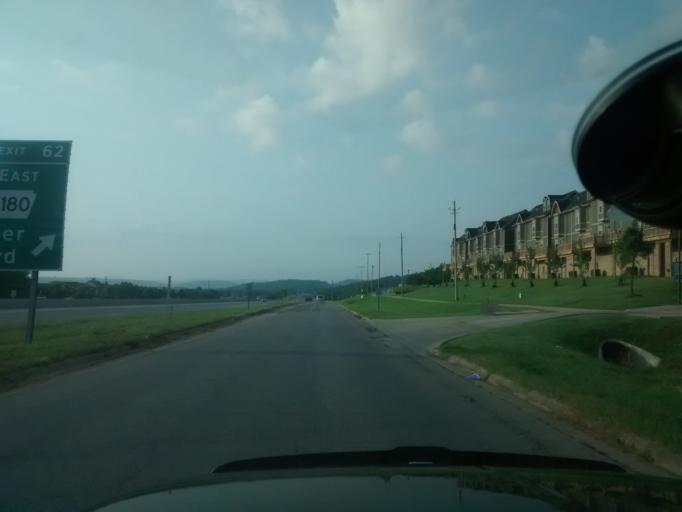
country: US
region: Arkansas
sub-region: Washington County
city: Fayetteville
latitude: 36.0624
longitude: -94.1995
